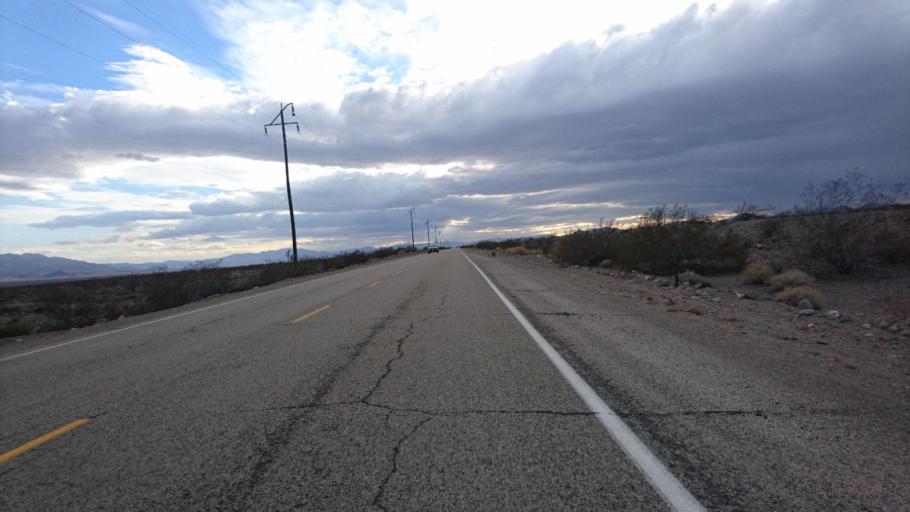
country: US
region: California
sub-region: San Bernardino County
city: Needles
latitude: 34.6593
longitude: -115.3559
